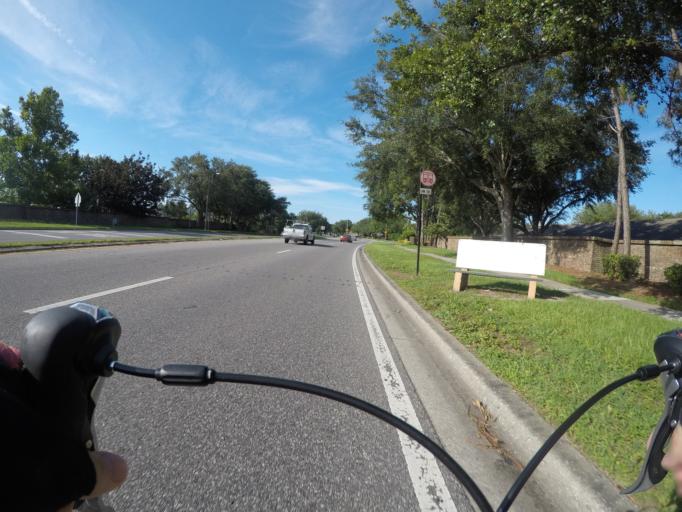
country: US
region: Florida
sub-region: Orange County
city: Meadow Woods
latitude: 28.3606
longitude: -81.3650
